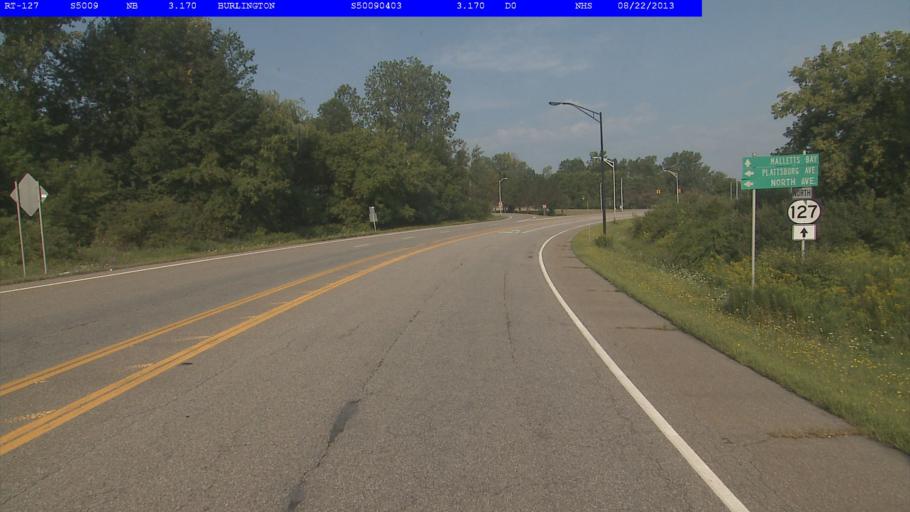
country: US
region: Vermont
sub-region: Chittenden County
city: Burlington
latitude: 44.5218
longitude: -73.2532
